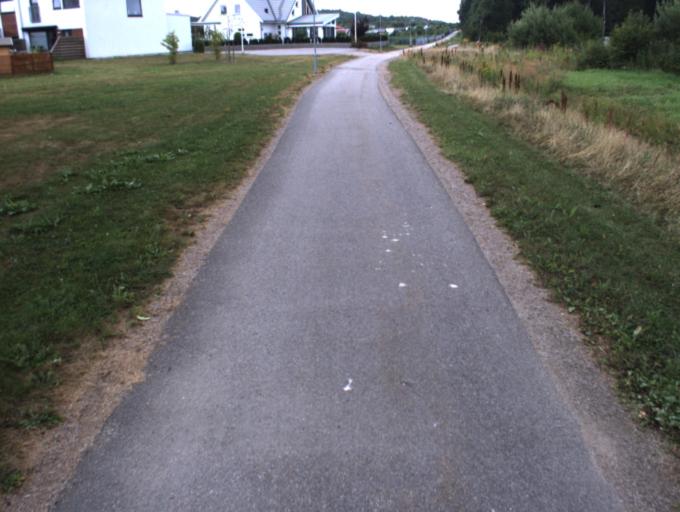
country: SE
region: Skane
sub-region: Helsingborg
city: Odakra
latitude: 56.0583
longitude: 12.7389
